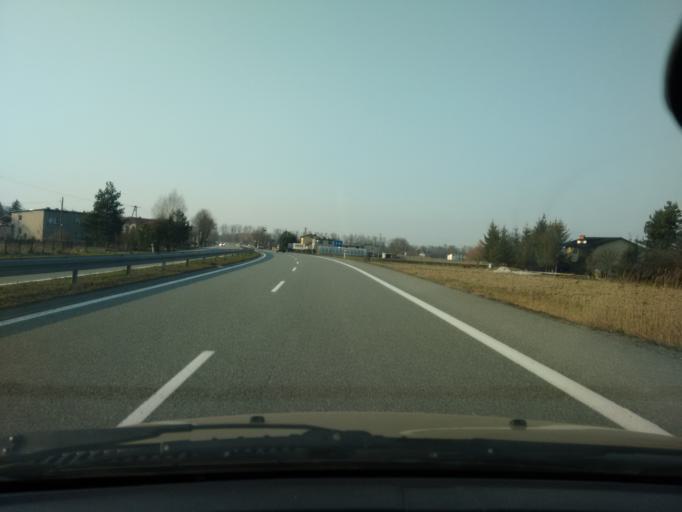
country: PL
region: Silesian Voivodeship
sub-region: Powiat cieszynski
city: Drogomysl
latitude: 49.8928
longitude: 18.7466
